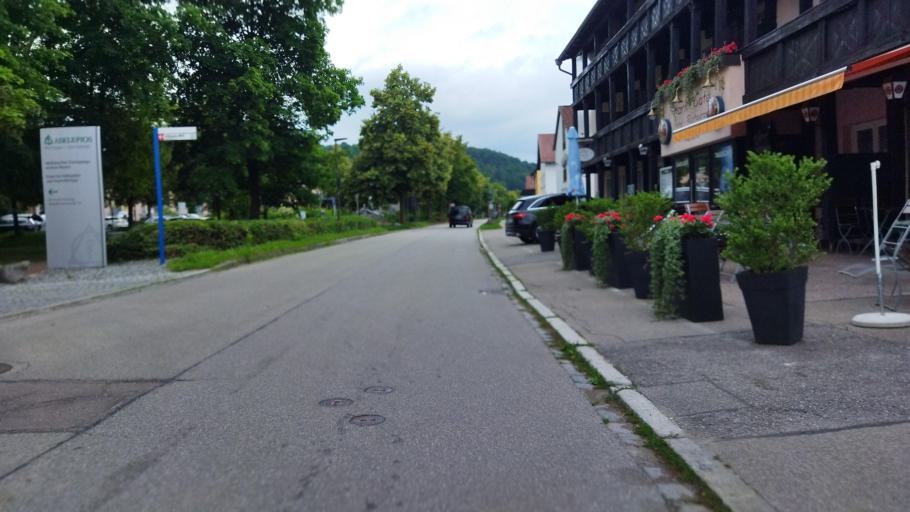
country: DE
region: Bavaria
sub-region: Lower Bavaria
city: Bad Abbach
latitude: 48.9331
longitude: 12.0373
